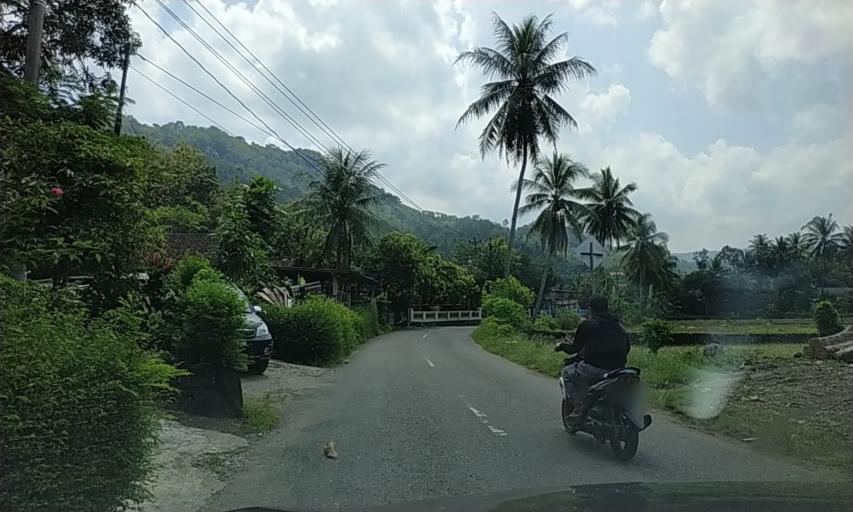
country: ID
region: Central Java
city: Gombong
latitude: -7.6316
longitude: 109.7156
